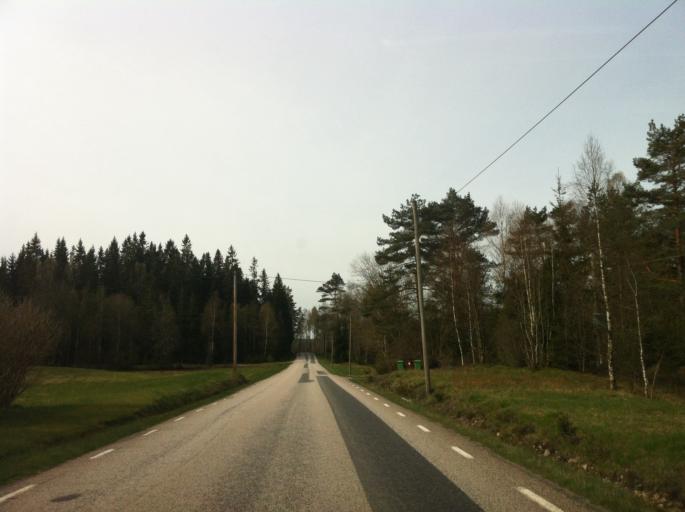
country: SE
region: Vaestra Goetaland
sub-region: Bollebygds Kommun
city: Bollebygd
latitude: 57.7488
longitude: 12.6106
